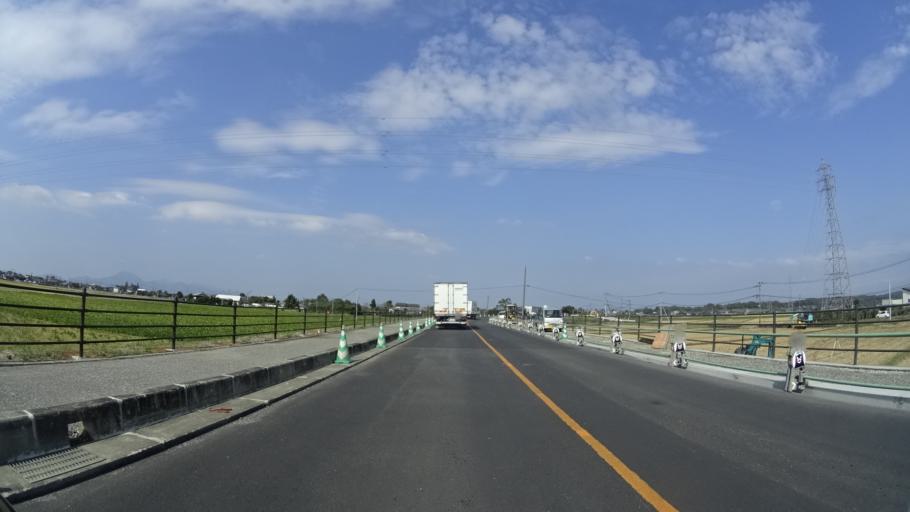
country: JP
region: Kumamoto
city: Kumamoto
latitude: 32.7350
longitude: 130.7720
